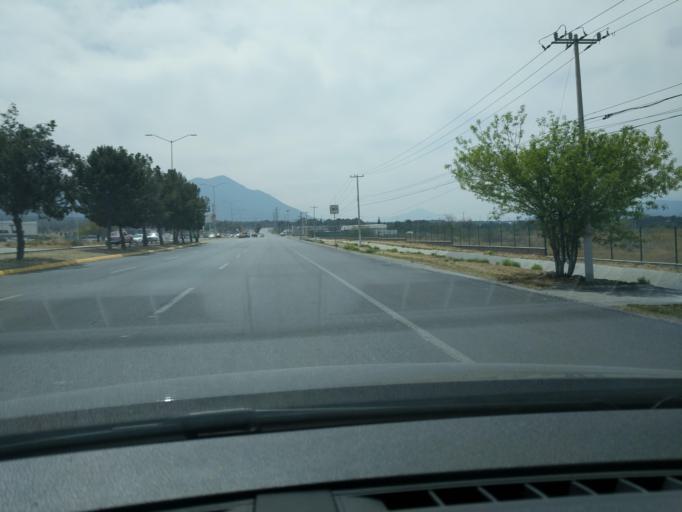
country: MX
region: Coahuila
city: Saltillo
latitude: 25.3550
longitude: -101.0214
